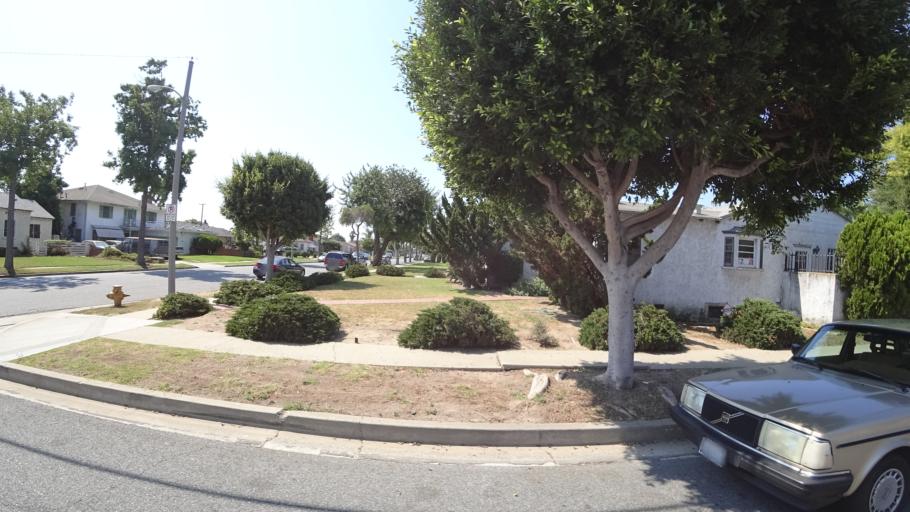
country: US
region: California
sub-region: Los Angeles County
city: Westmont
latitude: 33.9563
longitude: -118.3212
